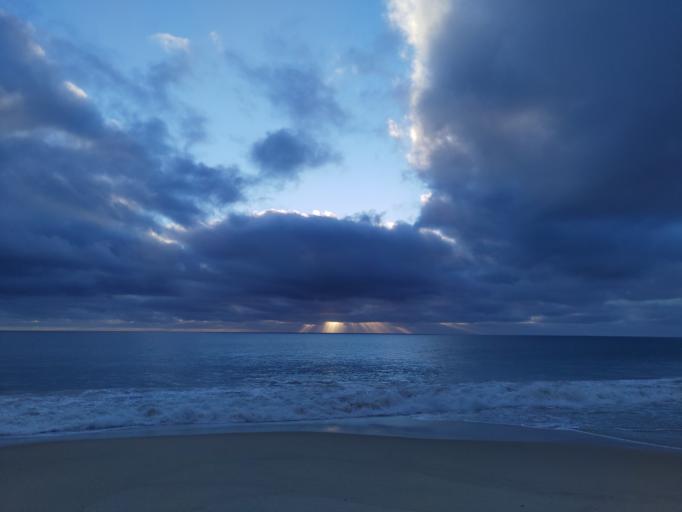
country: AU
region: Western Australia
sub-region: Waroona
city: Waroona
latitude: -32.8813
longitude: 115.6586
